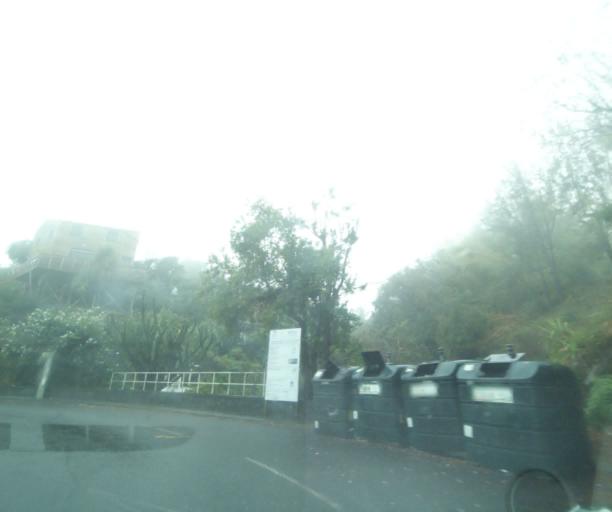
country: RE
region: Reunion
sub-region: Reunion
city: Saint-Paul
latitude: -20.9997
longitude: 55.3260
